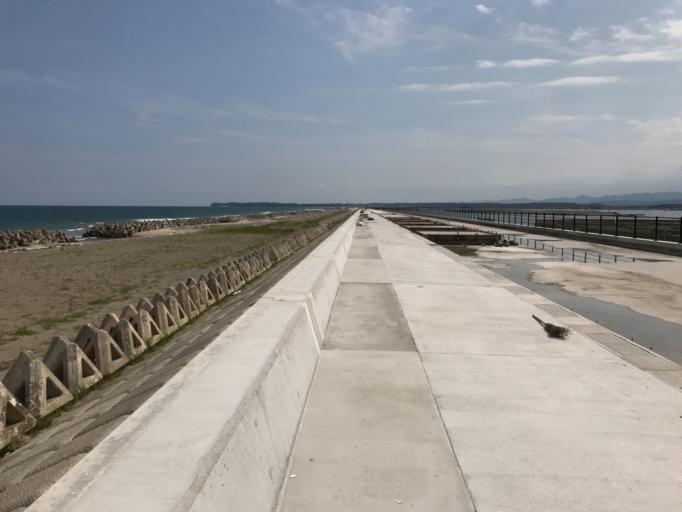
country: JP
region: Miyagi
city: Marumori
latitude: 37.8193
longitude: 140.9856
